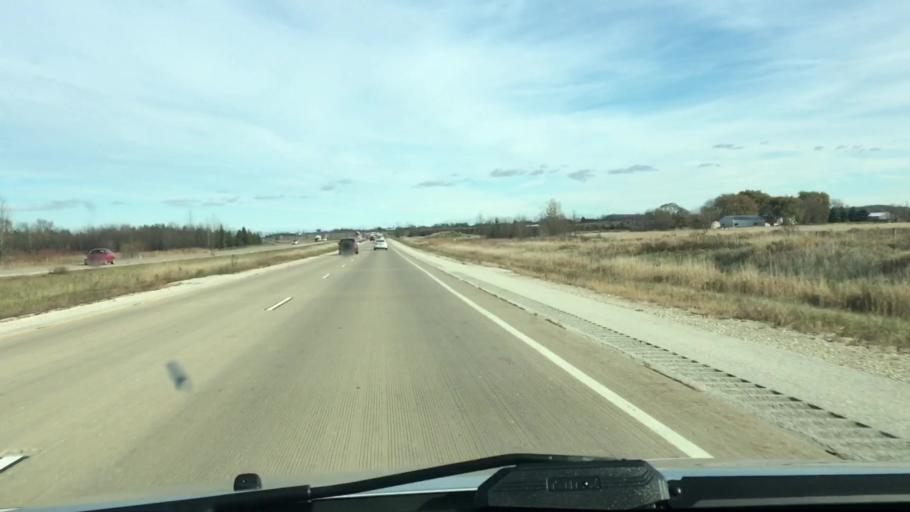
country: US
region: Wisconsin
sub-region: Kewaunee County
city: Luxemburg
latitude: 44.7160
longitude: -87.6462
